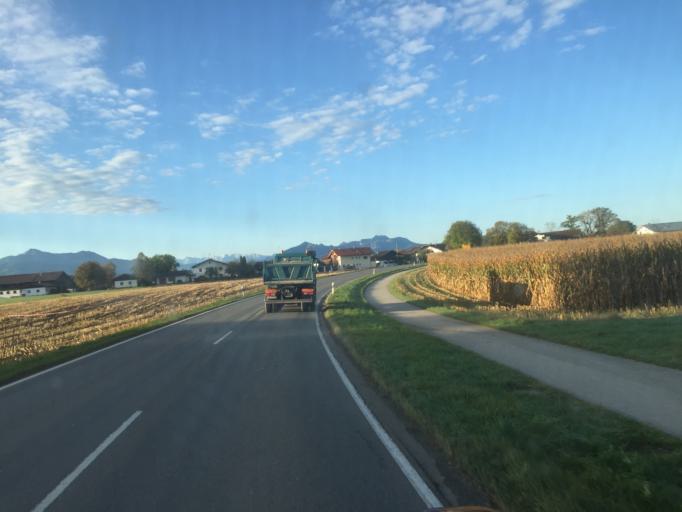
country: DE
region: Bavaria
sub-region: Upper Bavaria
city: Chieming
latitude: 47.9038
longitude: 12.5536
